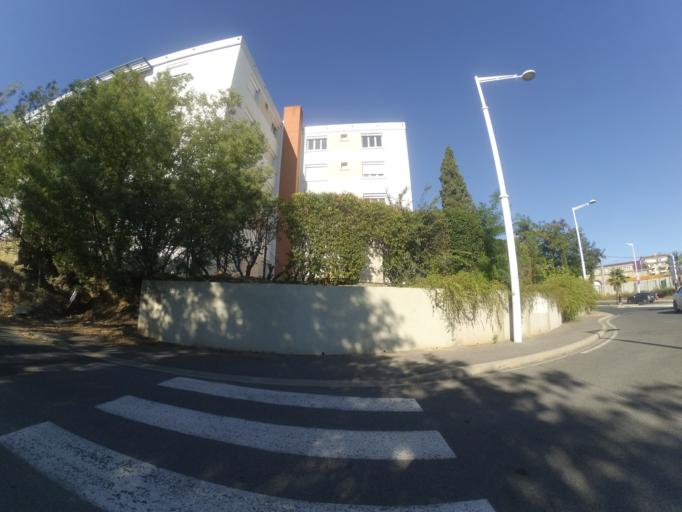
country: FR
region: Languedoc-Roussillon
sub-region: Departement des Pyrenees-Orientales
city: Perpignan
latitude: 42.6926
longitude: 2.8796
